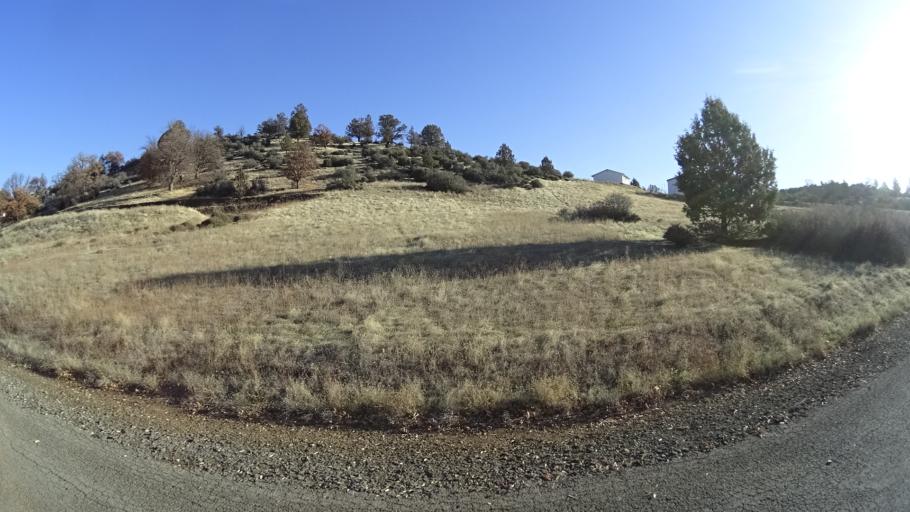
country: US
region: California
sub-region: Siskiyou County
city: Montague
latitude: 41.8922
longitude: -122.4924
